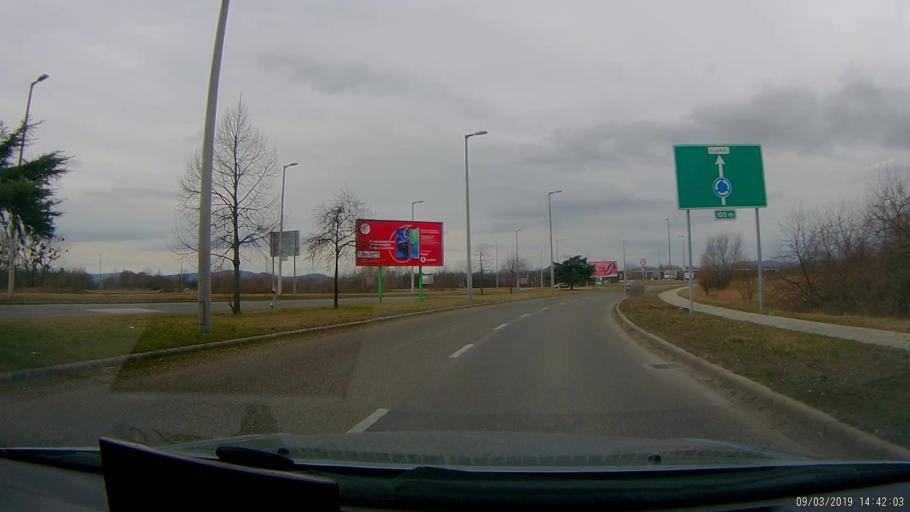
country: HU
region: Budapest
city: Budapest XV. keruelet
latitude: 47.5809
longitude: 19.1556
